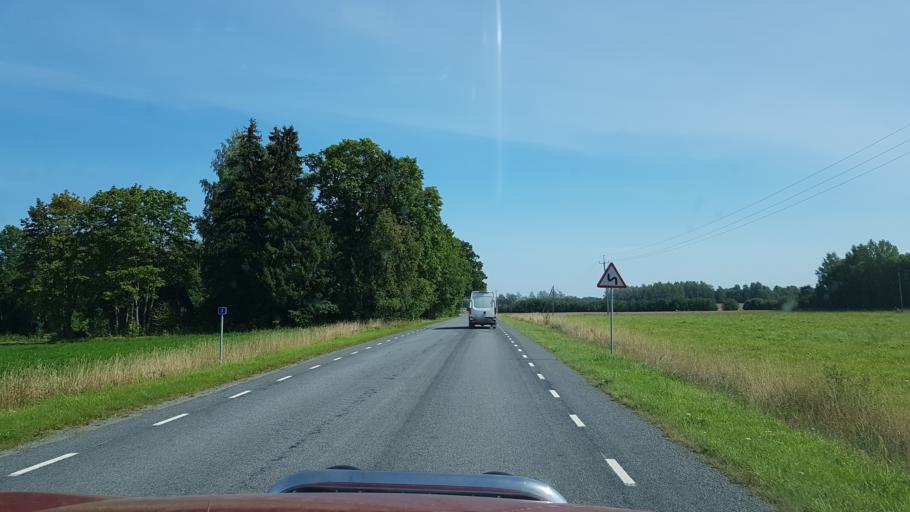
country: EE
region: Viljandimaa
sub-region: Suure-Jaani vald
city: Suure-Jaani
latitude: 58.4898
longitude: 25.5458
